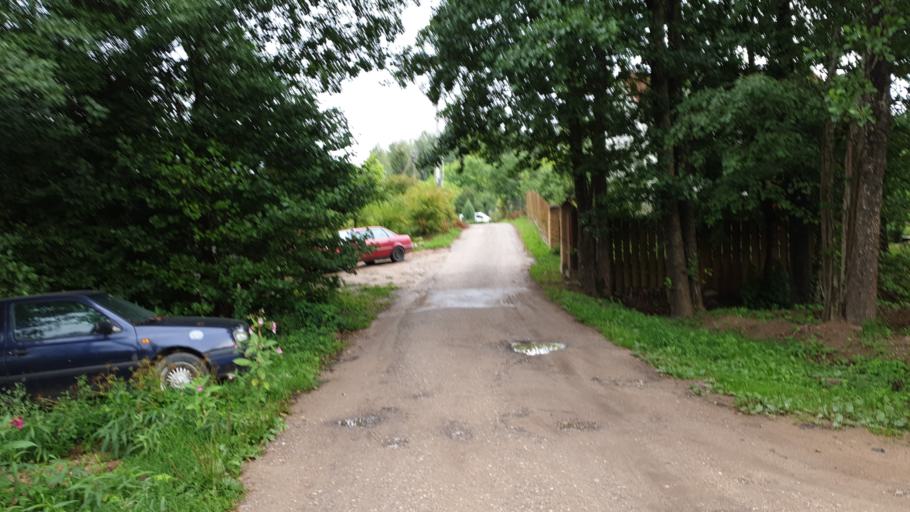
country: LT
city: Grigiskes
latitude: 54.7656
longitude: 25.0192
